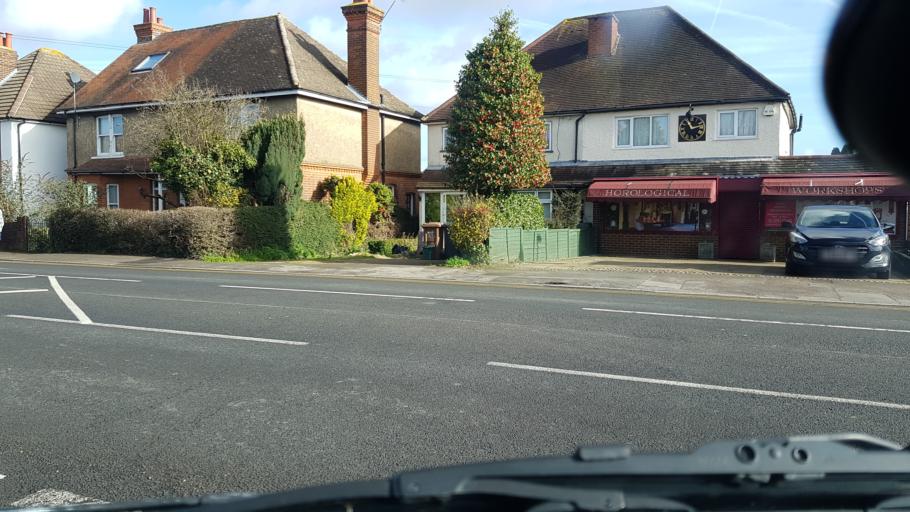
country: GB
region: England
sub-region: Surrey
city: Guildford
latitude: 51.2568
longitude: -0.5946
